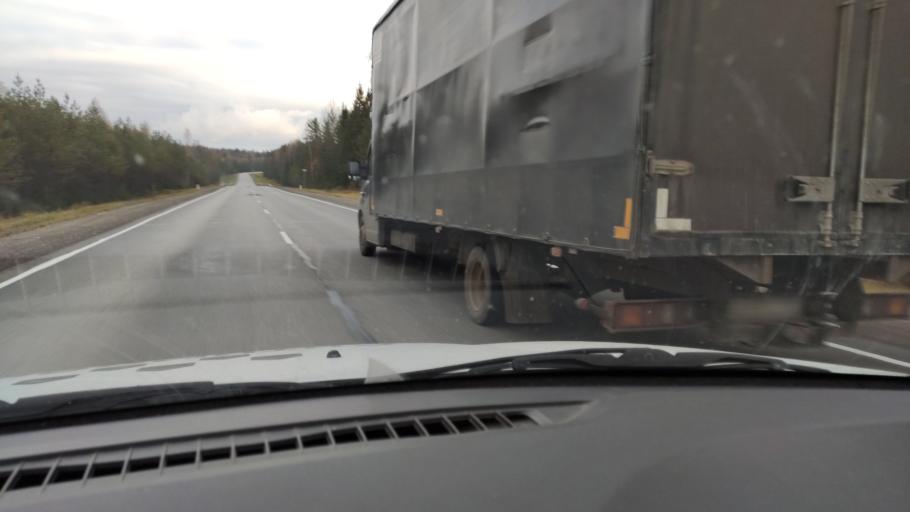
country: RU
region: Kirov
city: Chernaya Kholunitsa
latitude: 58.8239
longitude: 51.7942
